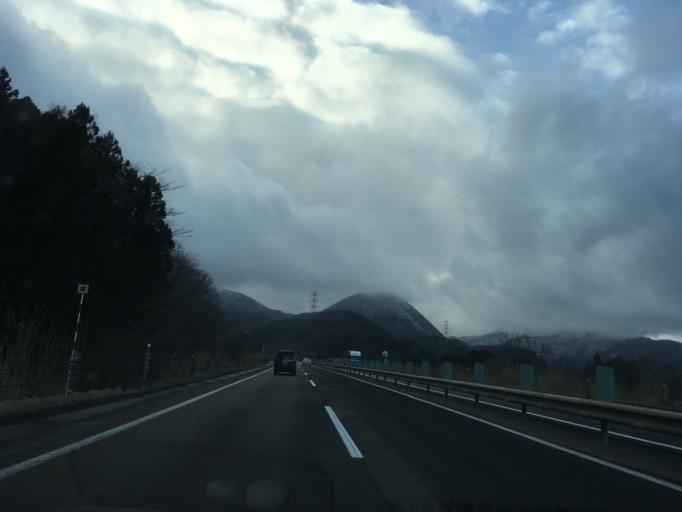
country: JP
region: Miyagi
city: Shiroishi
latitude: 38.1828
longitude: 140.6047
